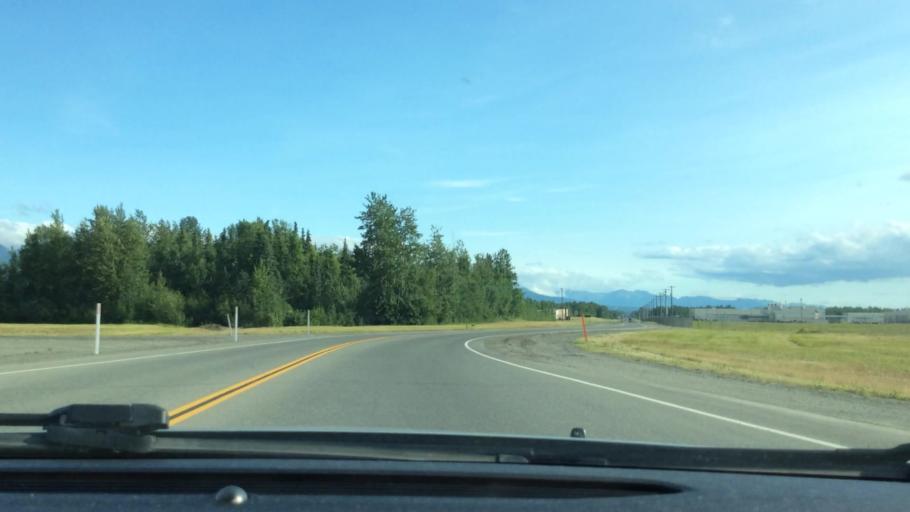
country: US
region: Alaska
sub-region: Anchorage Municipality
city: Anchorage
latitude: 61.2527
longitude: -149.7785
